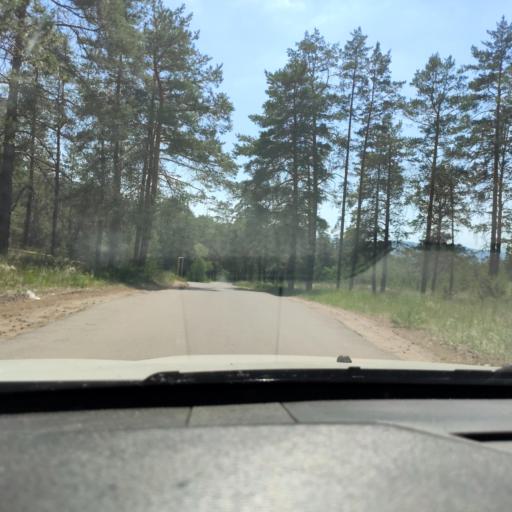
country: RU
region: Samara
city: Pribrezhnyy
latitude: 53.4803
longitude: 49.8254
